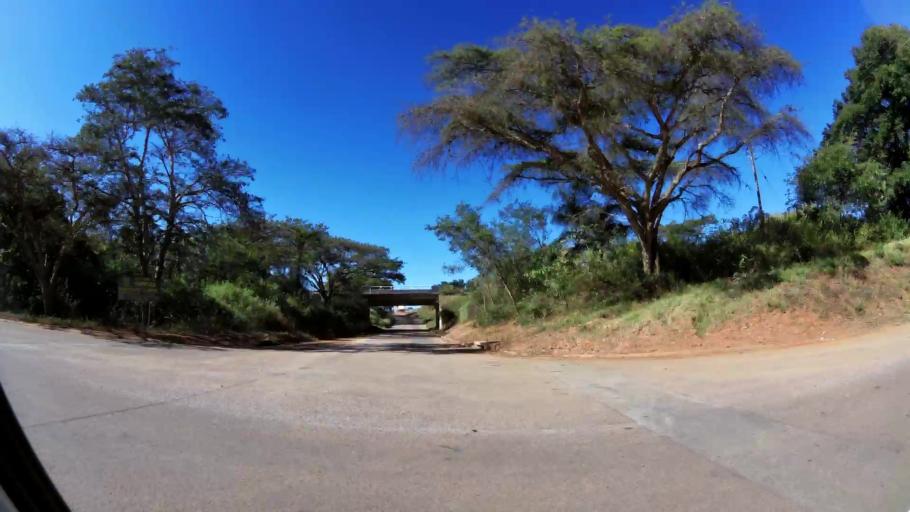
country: ZA
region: Limpopo
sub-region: Mopani District Municipality
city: Tzaneen
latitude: -23.8314
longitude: 30.1390
